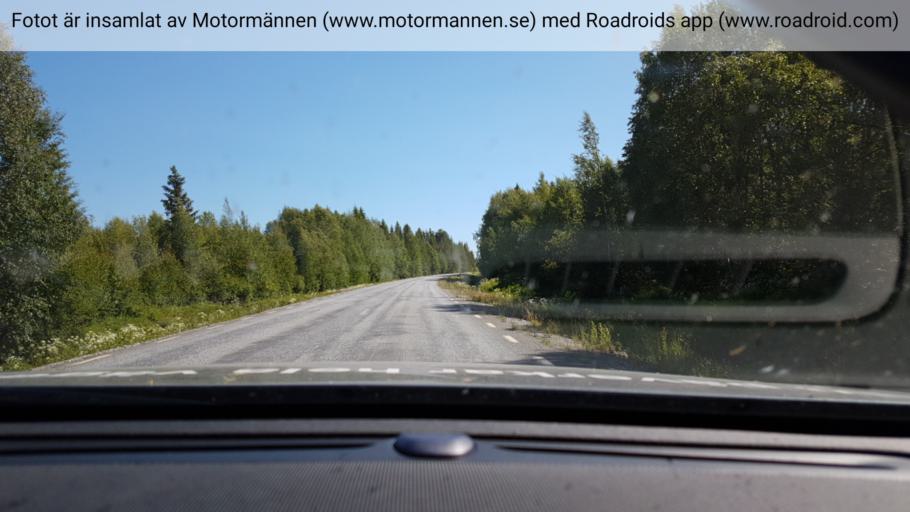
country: SE
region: Vaesterbotten
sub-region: Vilhelmina Kommun
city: Sjoberg
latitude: 64.7630
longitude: 16.1539
